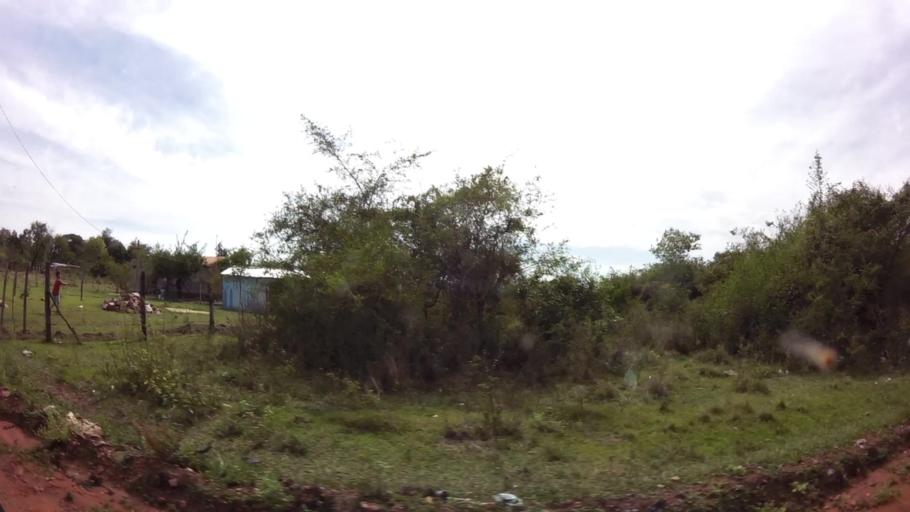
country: PY
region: Presidente Hayes
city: Villa Hayes
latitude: -25.1167
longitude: -57.4831
